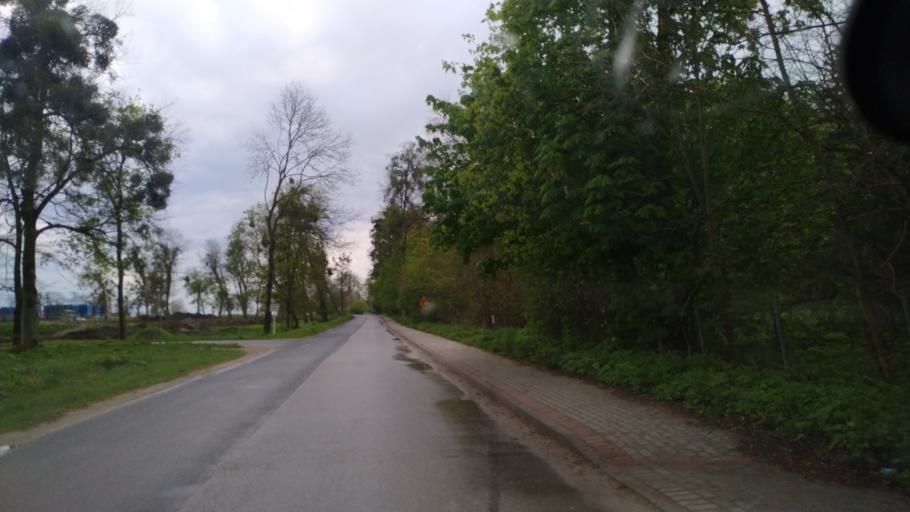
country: PL
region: Pomeranian Voivodeship
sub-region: Powiat starogardzki
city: Smetowo Graniczne
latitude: 53.7357
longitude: 18.6481
